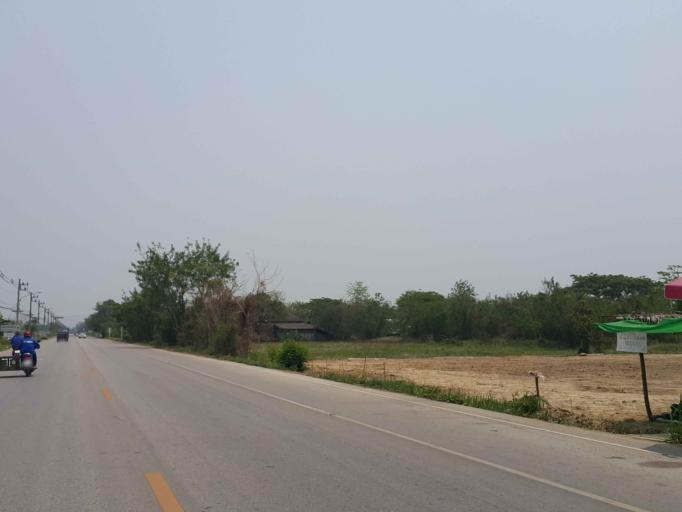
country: TH
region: Chiang Mai
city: San Kamphaeng
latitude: 18.7970
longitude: 99.1077
